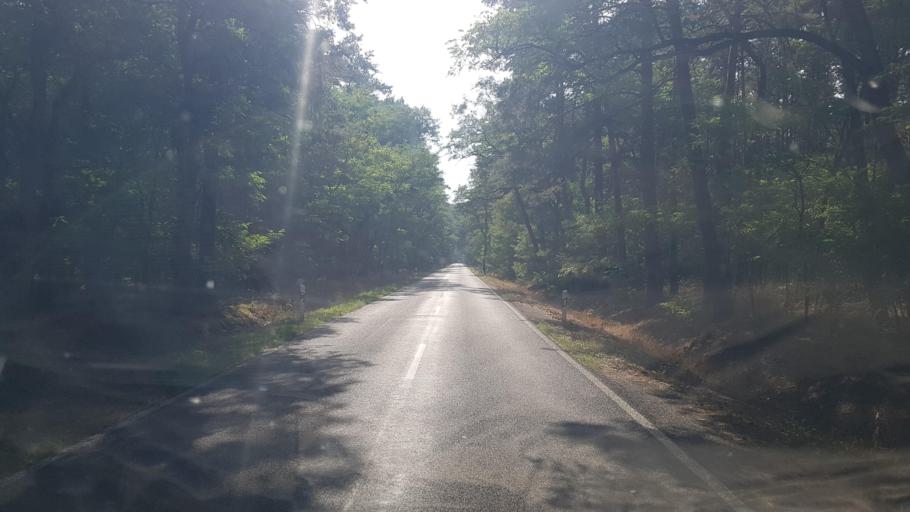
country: DE
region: Brandenburg
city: Dahme
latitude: 51.9523
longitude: 13.4105
